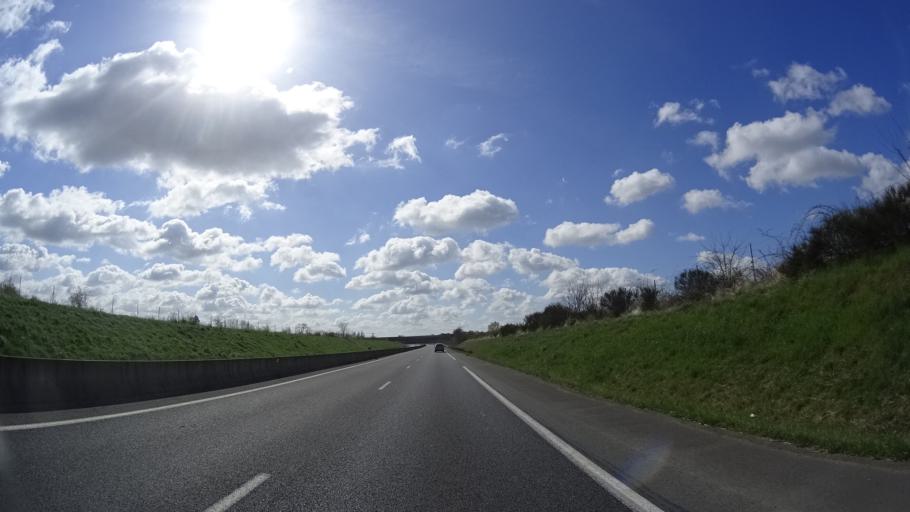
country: FR
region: Pays de la Loire
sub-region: Departement de Maine-et-Loire
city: Saint-Jean
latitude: 47.2995
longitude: -0.3897
